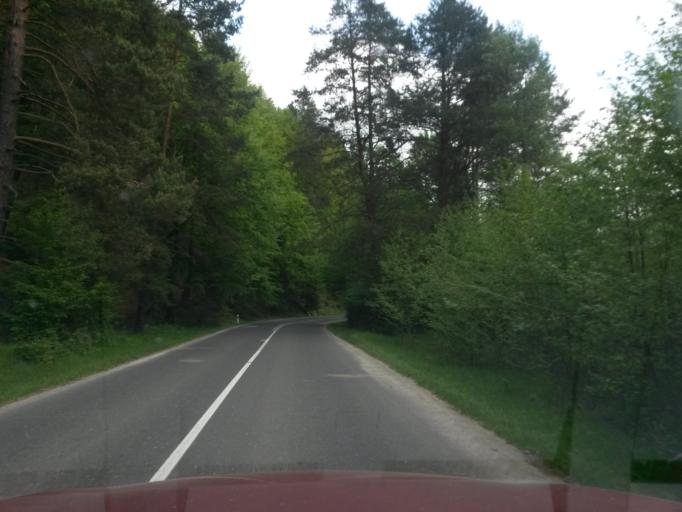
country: SK
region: Kosicky
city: Medzev
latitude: 48.7845
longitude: 20.7965
